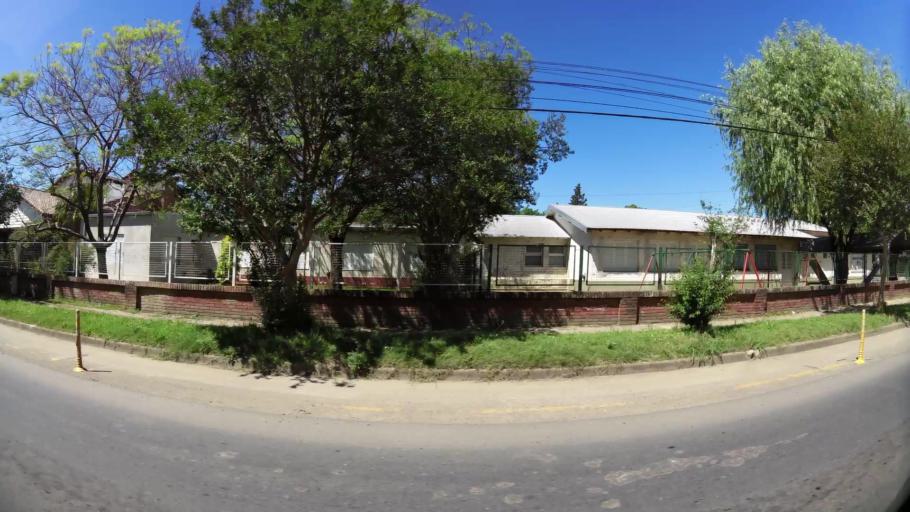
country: AR
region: Santa Fe
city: Esperanza
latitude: -31.4442
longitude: -60.9231
